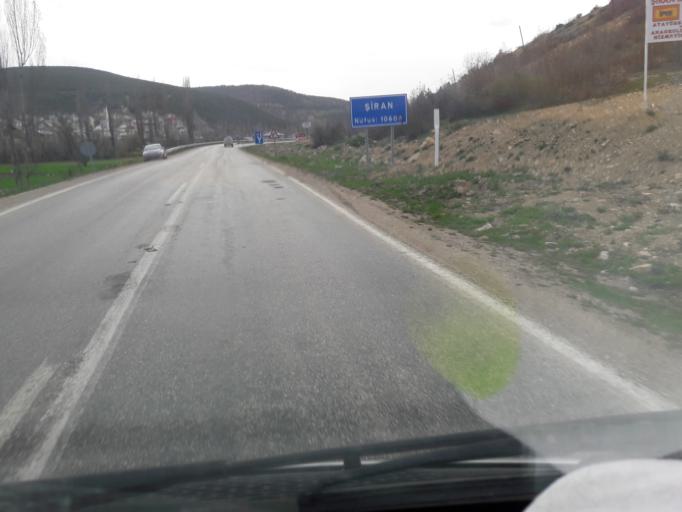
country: TR
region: Gumushane
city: Siran
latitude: 40.1767
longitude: 39.1390
